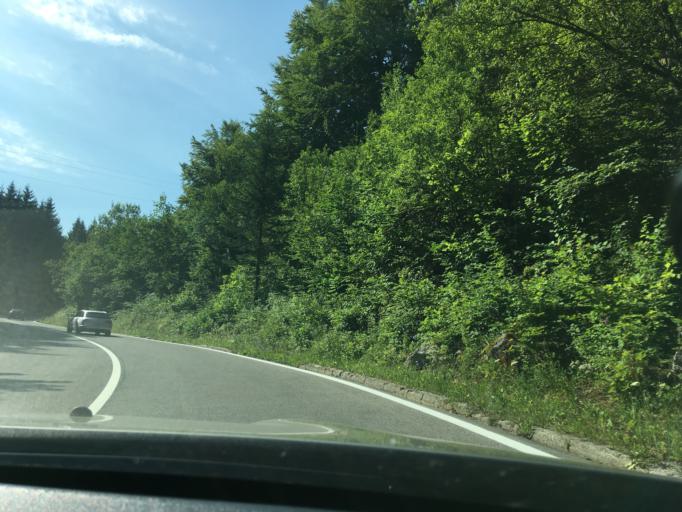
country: HR
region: Primorsko-Goranska
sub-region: Grad Delnice
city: Delnice
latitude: 45.4045
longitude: 14.8114
